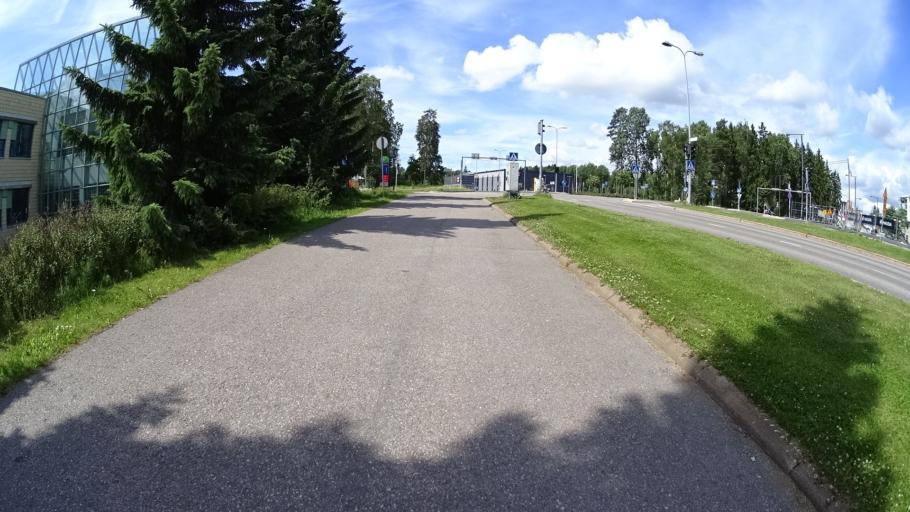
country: FI
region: Uusimaa
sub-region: Helsinki
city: Teekkarikylae
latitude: 60.2590
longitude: 24.8440
